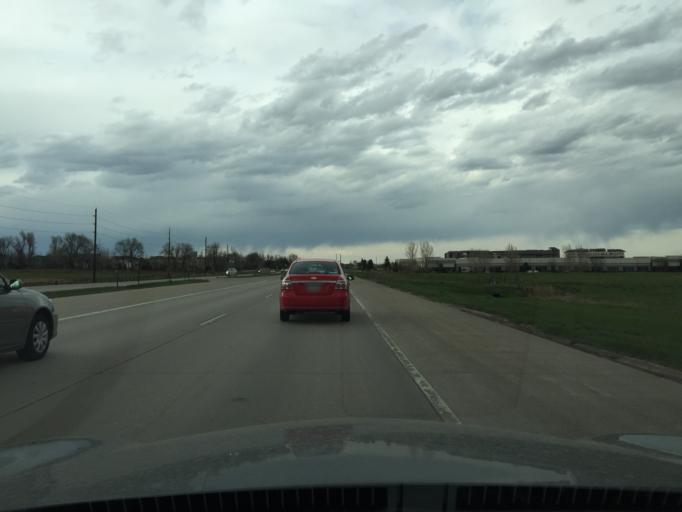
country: US
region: Colorado
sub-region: Boulder County
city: Lafayette
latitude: 39.9628
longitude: -105.0901
